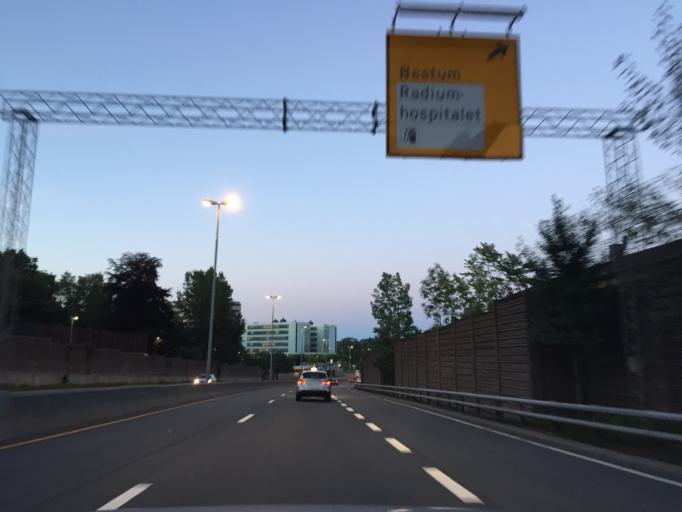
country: NO
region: Oslo
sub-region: Oslo
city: Sjolyststranda
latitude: 59.9279
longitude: 10.6561
